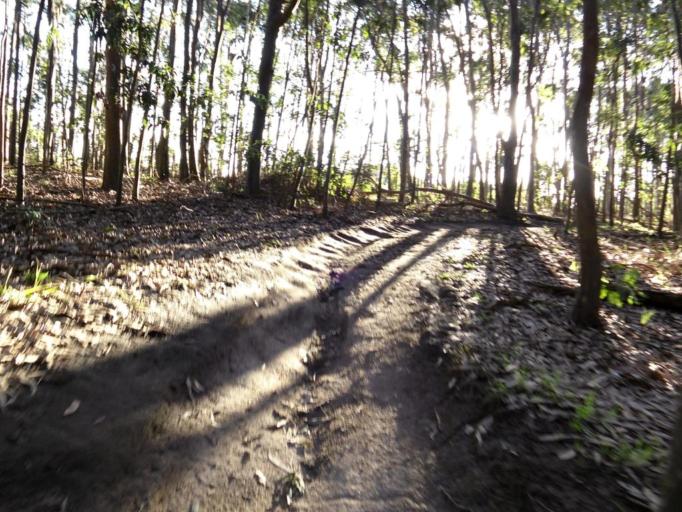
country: AU
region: Victoria
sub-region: Casey
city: Narre Warren North
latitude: -37.9665
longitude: 145.2904
